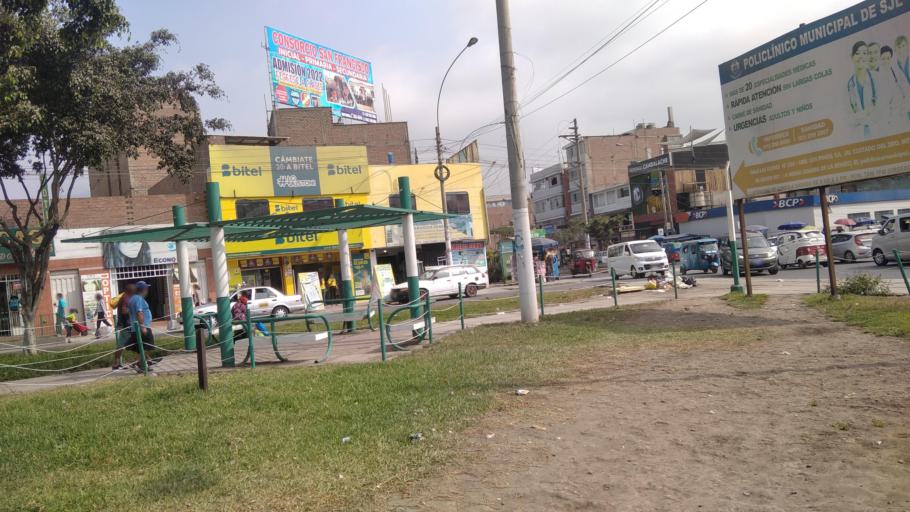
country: PE
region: Lima
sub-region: Lima
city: Independencia
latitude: -11.9700
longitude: -77.0057
